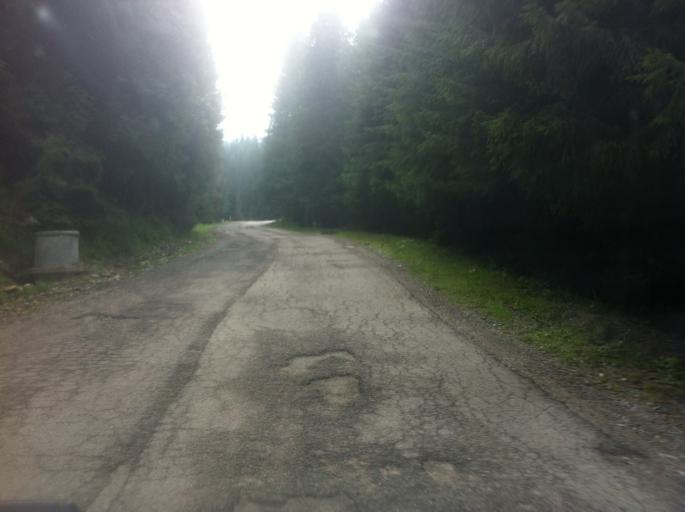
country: RO
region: Hunedoara
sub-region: Oras Petrila
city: Petrila
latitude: 45.4080
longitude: 23.5584
